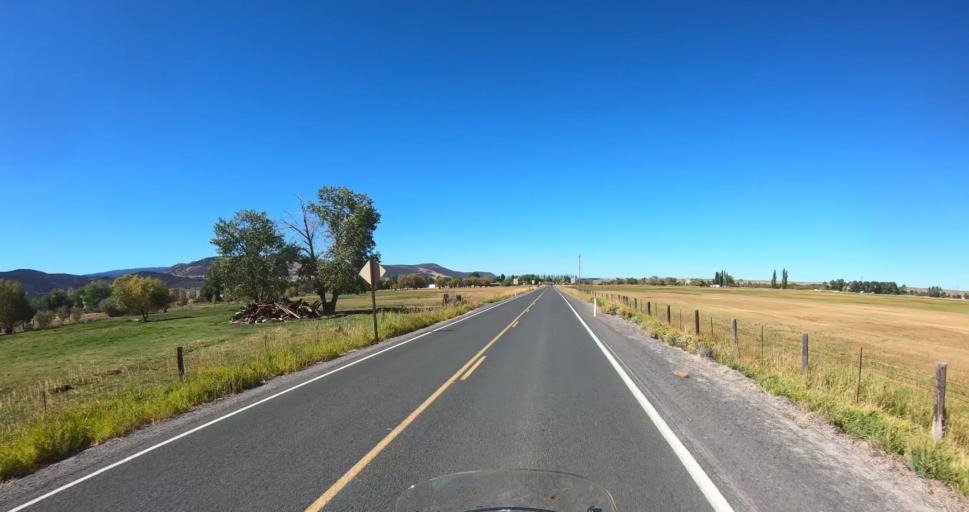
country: US
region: Oregon
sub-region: Lake County
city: Lakeview
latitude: 42.6895
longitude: -120.5328
